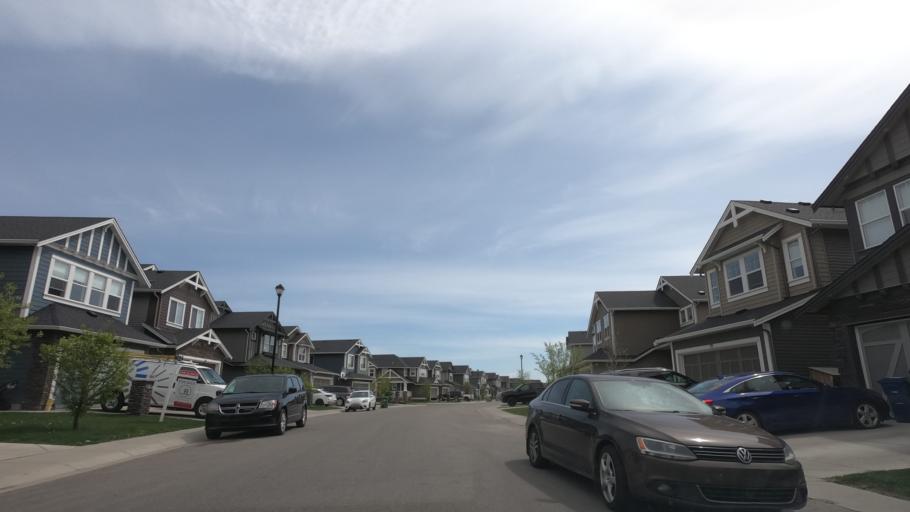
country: CA
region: Alberta
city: Airdrie
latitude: 51.3068
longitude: -114.0350
